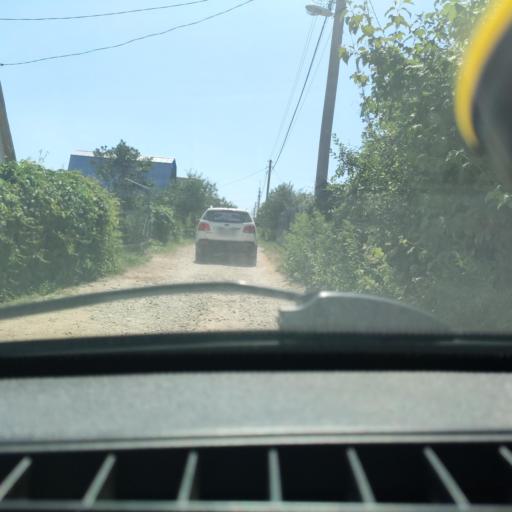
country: RU
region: Samara
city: Tol'yatti
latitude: 53.5933
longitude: 49.3051
